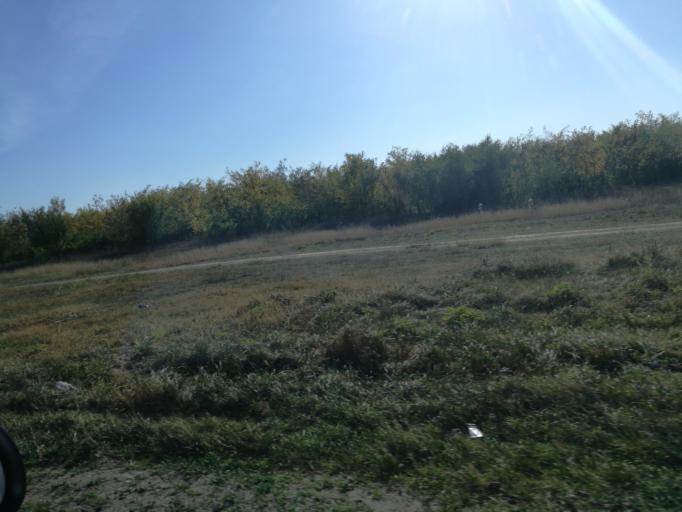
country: RO
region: Giurgiu
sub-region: Comuna Joita
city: Bacu
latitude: 44.4784
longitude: 25.9016
